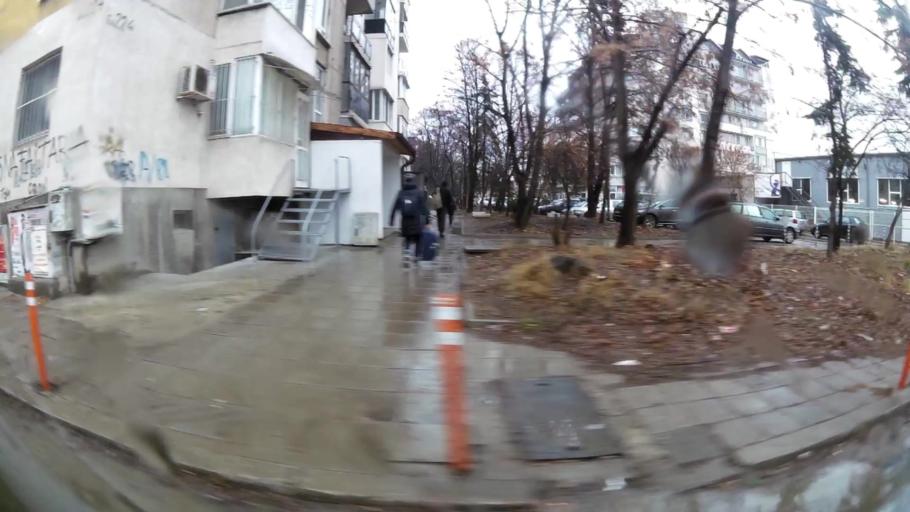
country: BG
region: Sofia-Capital
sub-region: Stolichna Obshtina
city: Sofia
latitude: 42.6469
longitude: 23.3749
